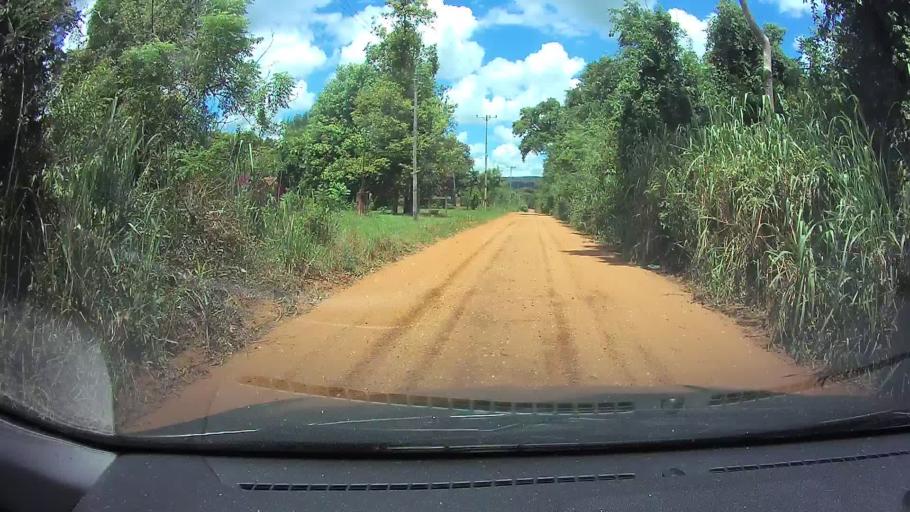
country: PY
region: Paraguari
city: La Colmena
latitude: -25.9103
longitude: -56.7945
